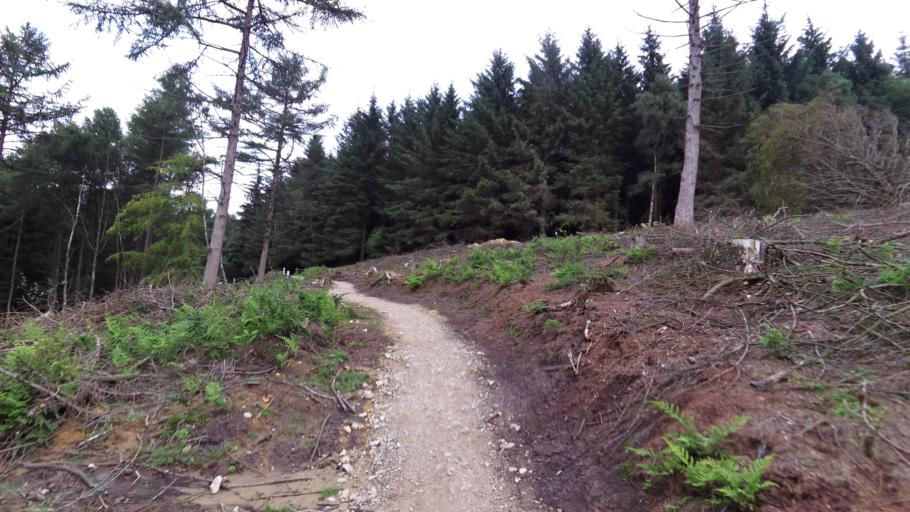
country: GB
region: England
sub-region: North Yorkshire
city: Thornton Dale
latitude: 54.2791
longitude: -0.6853
